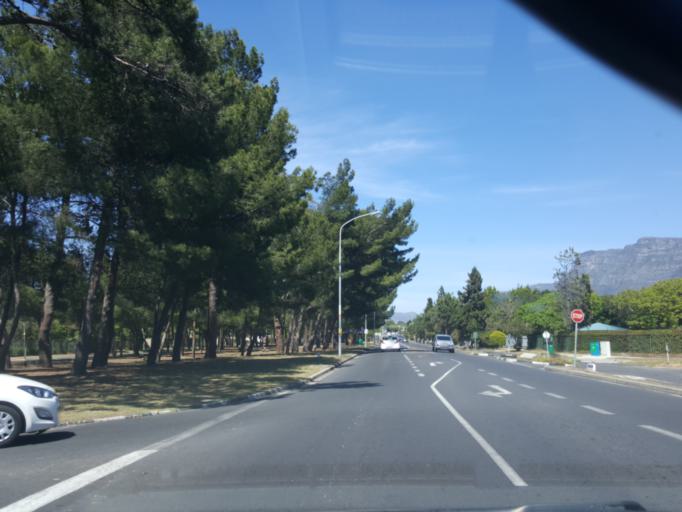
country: ZA
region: Western Cape
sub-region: City of Cape Town
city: Rosebank
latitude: -33.9383
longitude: 18.5039
